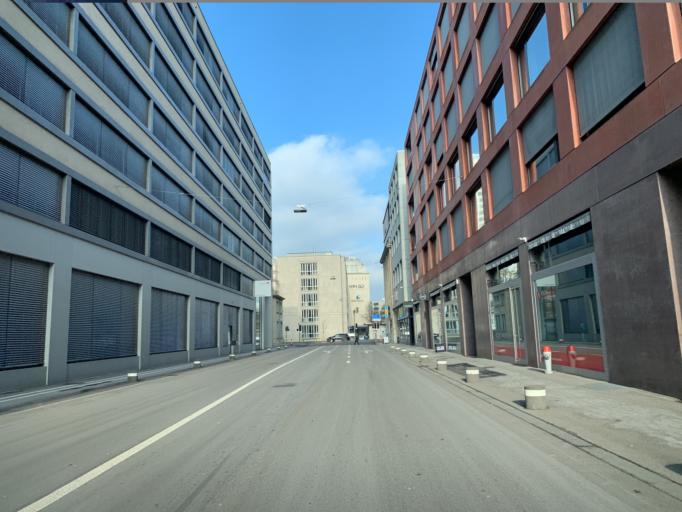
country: CH
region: Zurich
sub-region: Bezirk Winterthur
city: Stadt Winterthur (Kreis 1)
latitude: 47.4975
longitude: 8.7199
